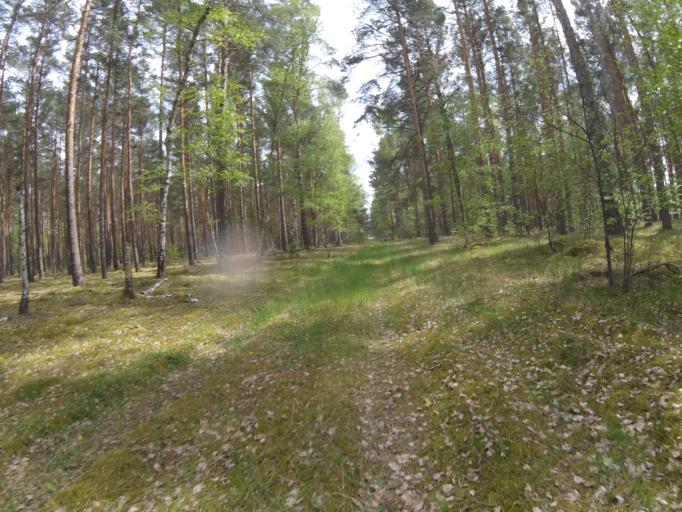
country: DE
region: Brandenburg
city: Schwerin
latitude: 52.1886
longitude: 13.6250
